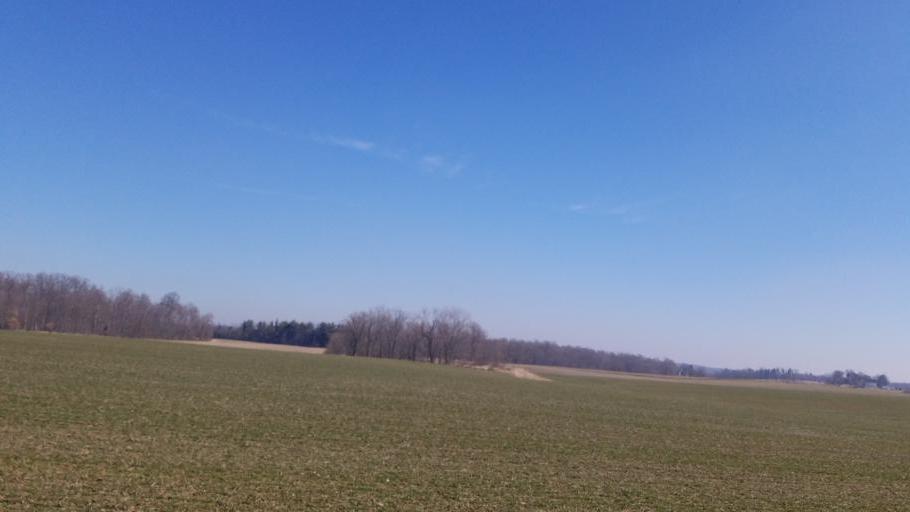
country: US
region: Ohio
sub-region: Richland County
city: Shelby
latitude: 40.8808
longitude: -82.5465
